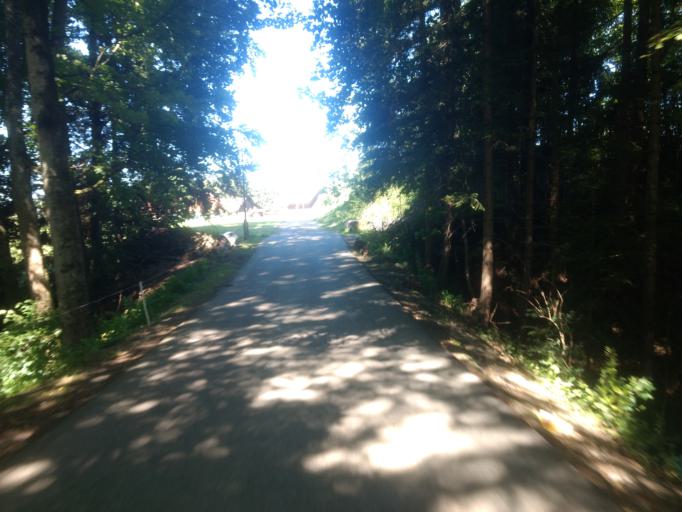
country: CH
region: Zurich
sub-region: Bezirk Horgen
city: Muehlehalde
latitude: 47.2747
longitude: 8.5126
